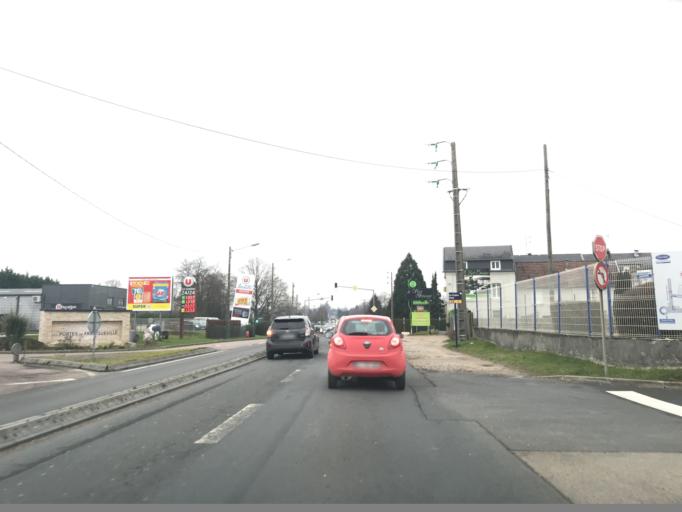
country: FR
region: Haute-Normandie
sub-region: Departement de la Seine-Maritime
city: Boos
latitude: 49.3975
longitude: 1.1788
